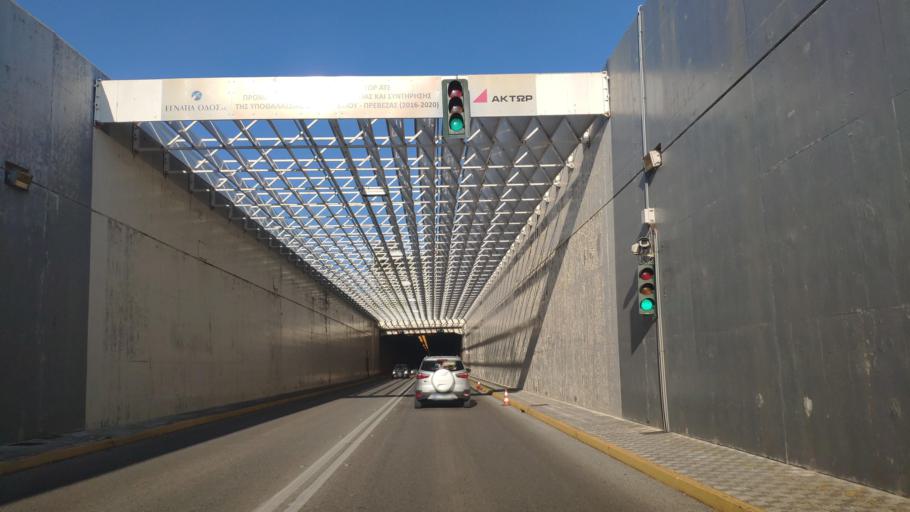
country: GR
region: Epirus
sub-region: Nomos Prevezis
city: Preveza
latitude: 38.9493
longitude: 20.7462
